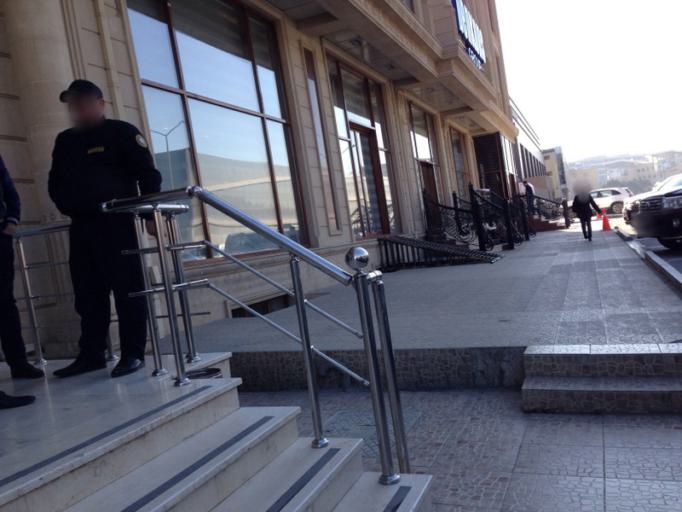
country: AZ
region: Baki
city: Baku
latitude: 40.4070
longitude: 49.8632
